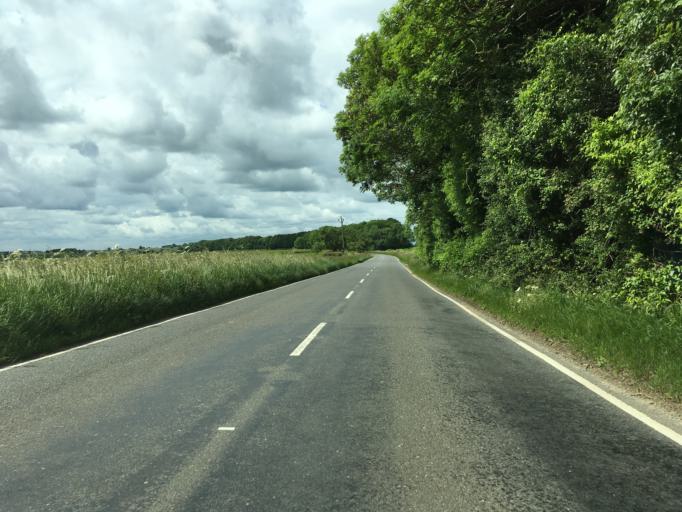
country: GB
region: England
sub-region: Oxfordshire
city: Chipping Norton
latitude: 51.9147
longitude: -1.5486
